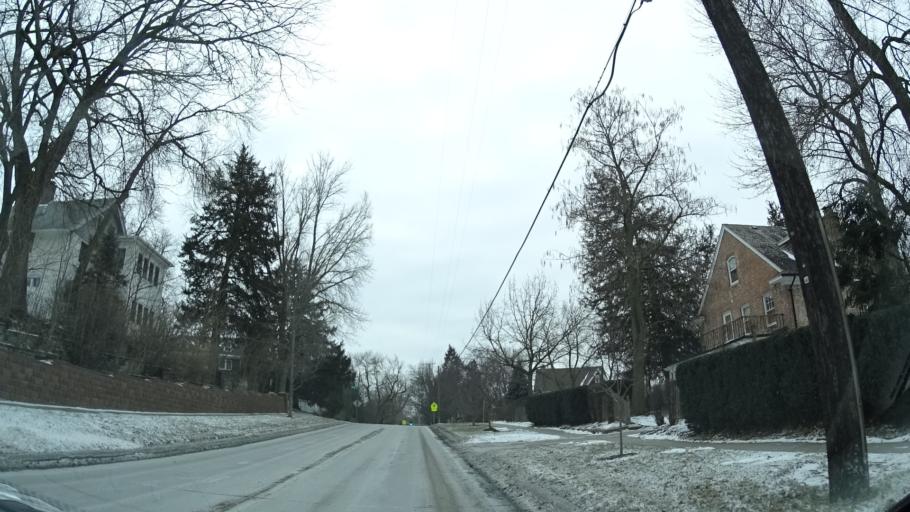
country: US
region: Nebraska
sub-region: Douglas County
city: Omaha
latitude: 41.2638
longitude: -95.9951
